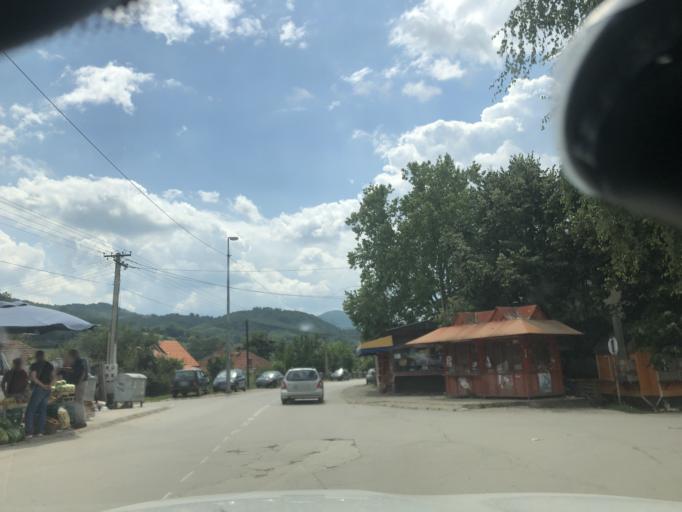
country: RS
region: Central Serbia
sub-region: Jablanicki Okrug
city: Medvega
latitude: 42.8437
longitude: 21.5872
